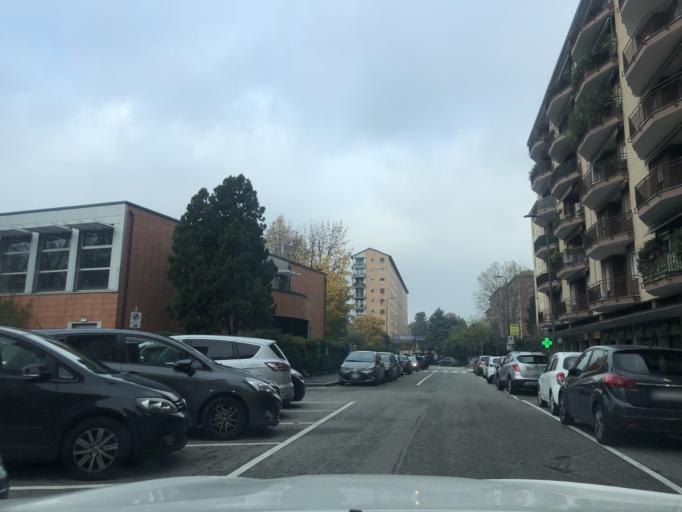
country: IT
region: Lombardy
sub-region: Citta metropolitana di Milano
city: Baranzate
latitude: 45.4941
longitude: 9.1256
